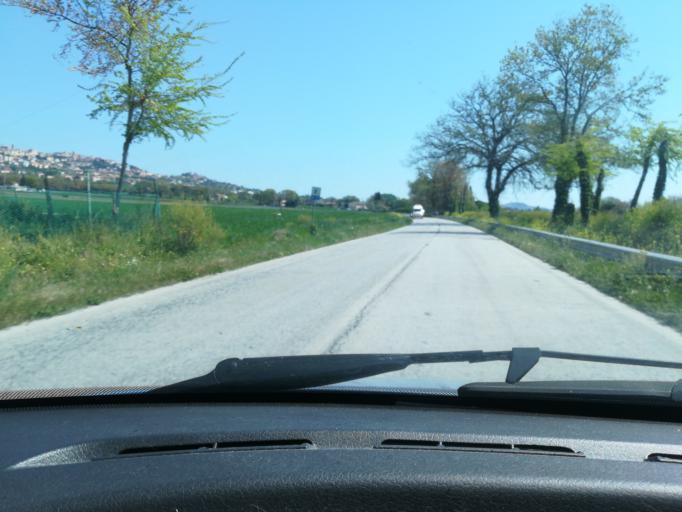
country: IT
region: The Marches
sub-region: Provincia di Ancona
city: Campocavallo
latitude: 43.4553
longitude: 13.5195
